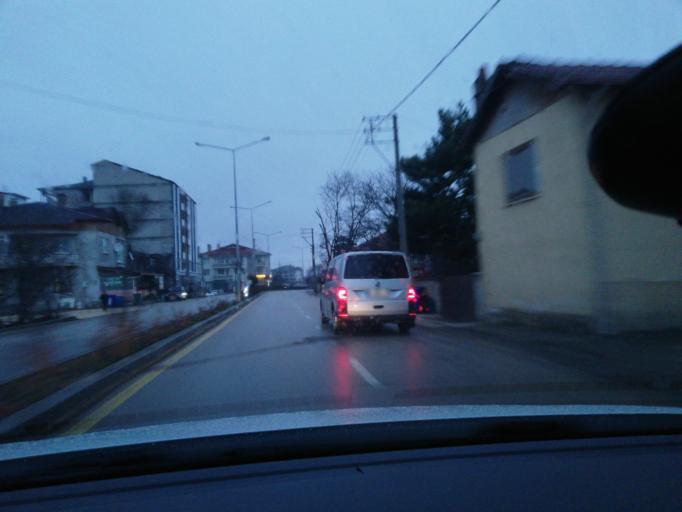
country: TR
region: Bolu
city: Bolu
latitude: 40.7299
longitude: 31.5788
